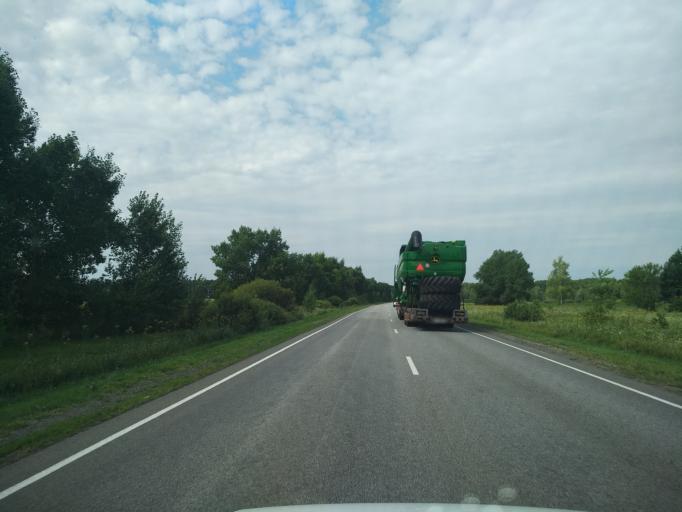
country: RU
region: Voronezj
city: Pereleshinskiy
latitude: 51.8688
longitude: 40.3827
